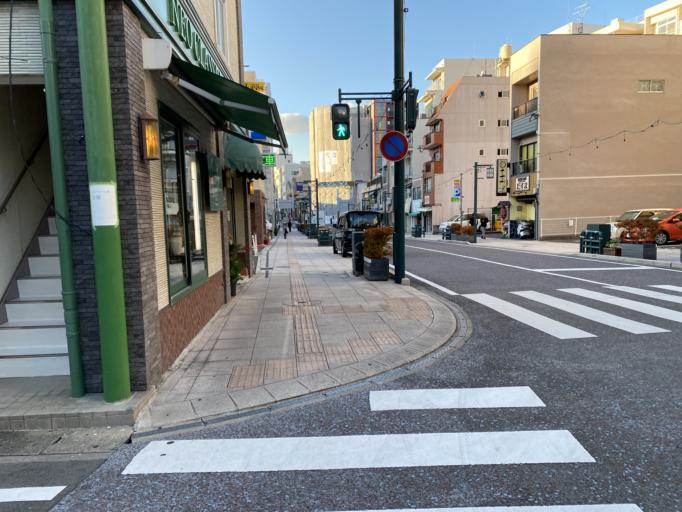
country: JP
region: Nagasaki
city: Nagasaki-shi
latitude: 32.7400
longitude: 129.8762
